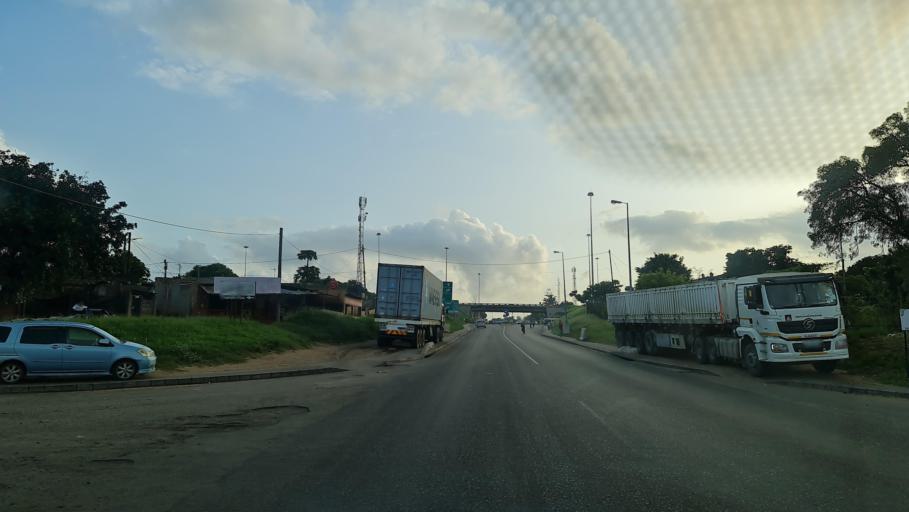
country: MZ
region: Maputo City
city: Maputo
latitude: -25.9455
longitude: 32.5390
